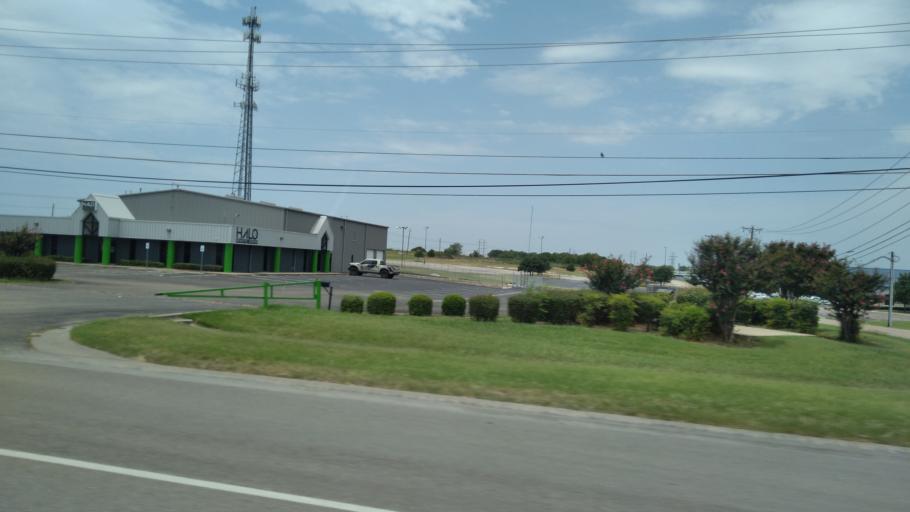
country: US
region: Texas
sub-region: McLennan County
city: Beverly Hills
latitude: 31.4967
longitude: -97.1649
